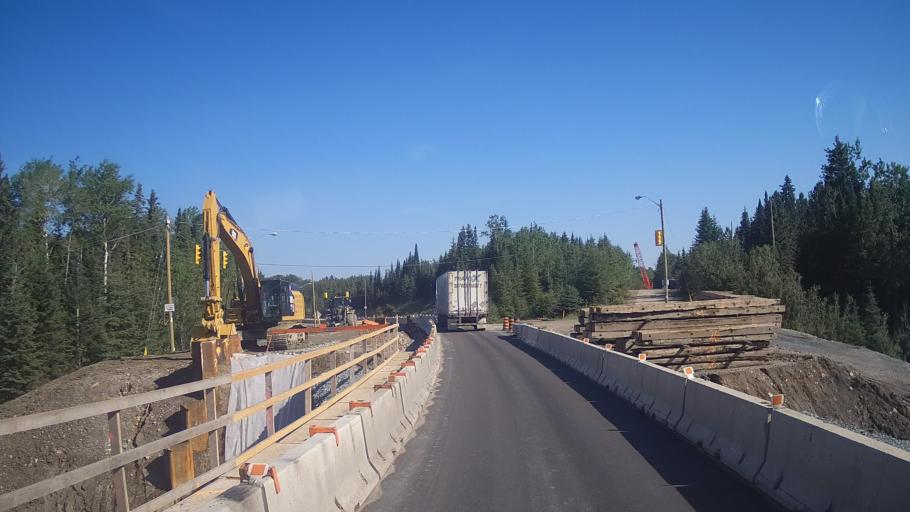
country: CA
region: Ontario
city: Dryden
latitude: 49.6856
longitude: -92.4928
